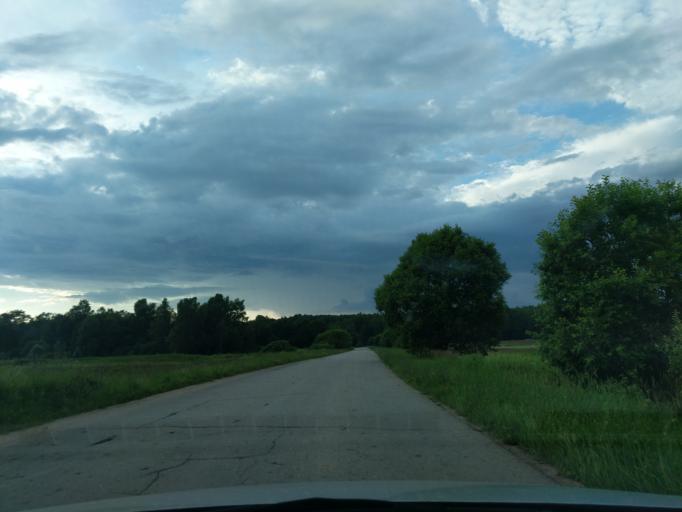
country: RU
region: Kaluga
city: Myatlevo
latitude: 54.8364
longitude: 35.6366
